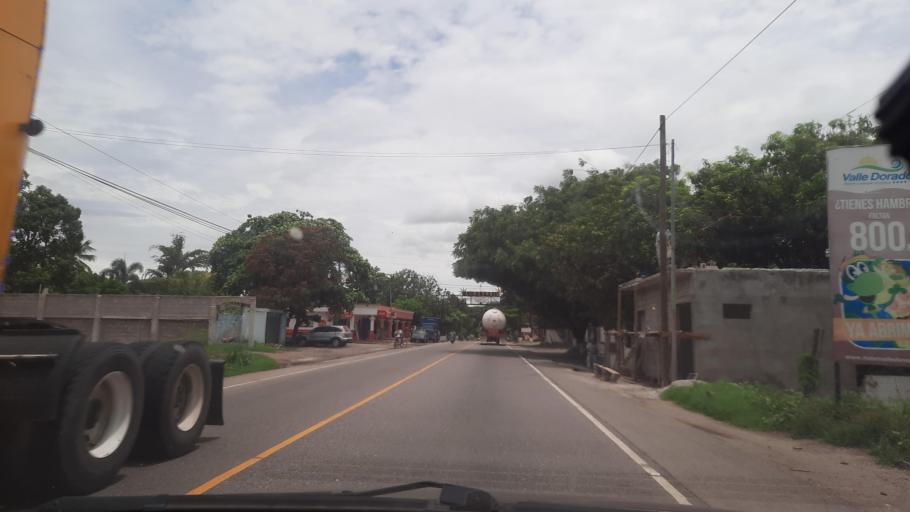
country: GT
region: Zacapa
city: Rio Hondo
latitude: 15.0857
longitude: -89.4720
